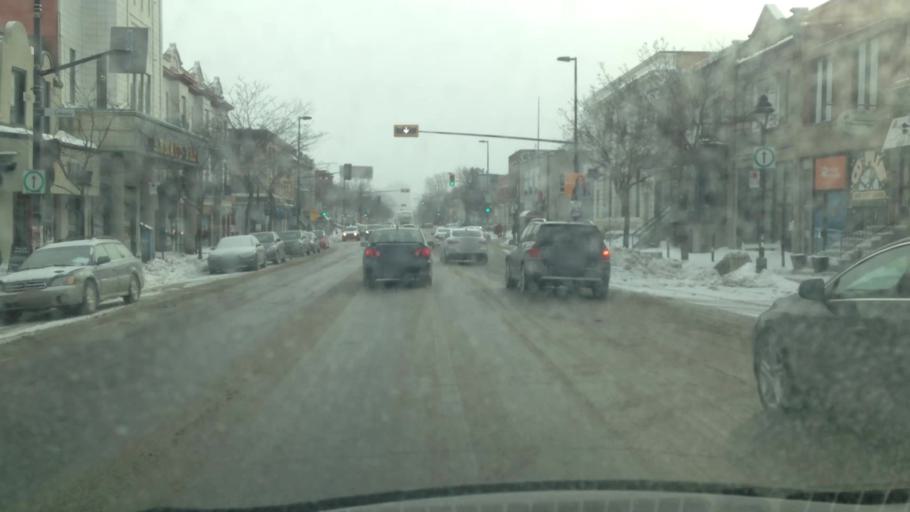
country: CA
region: Quebec
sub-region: Montreal
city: Montreal
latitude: 45.5200
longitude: -73.5968
